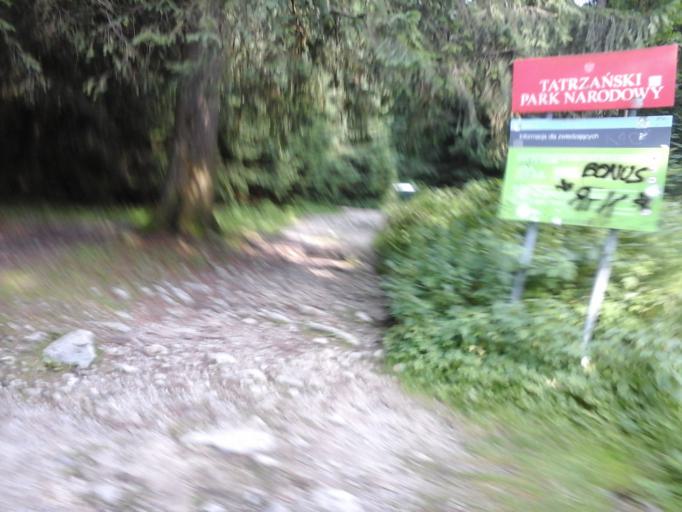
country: PL
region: Lesser Poland Voivodeship
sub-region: Powiat tatrzanski
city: Zakopane
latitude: 49.2791
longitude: 19.9812
